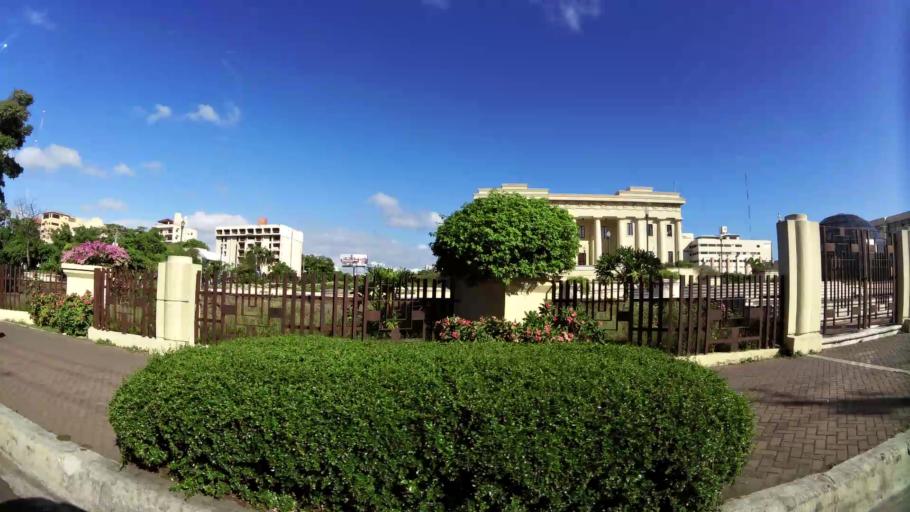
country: DO
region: Nacional
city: Ciudad Nueva
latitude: 18.4610
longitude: -69.9072
